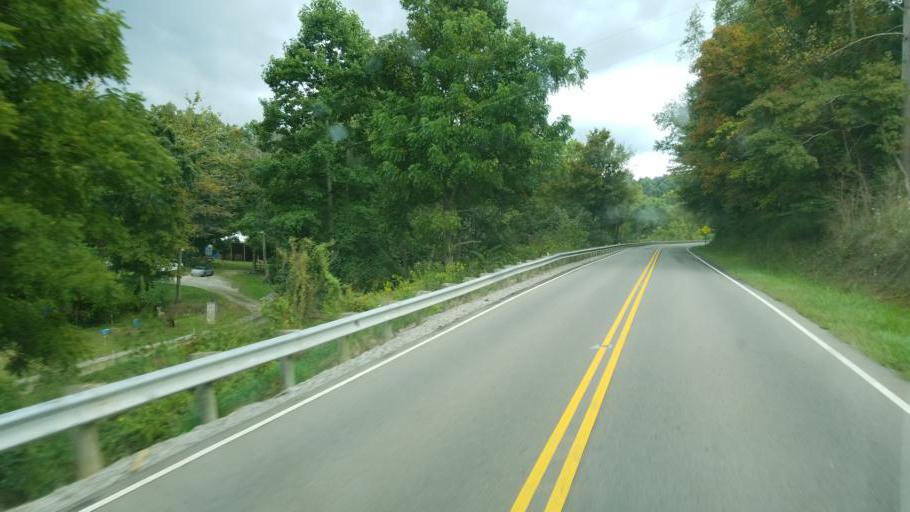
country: US
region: Ohio
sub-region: Jackson County
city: Jackson
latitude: 39.0035
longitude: -82.6500
